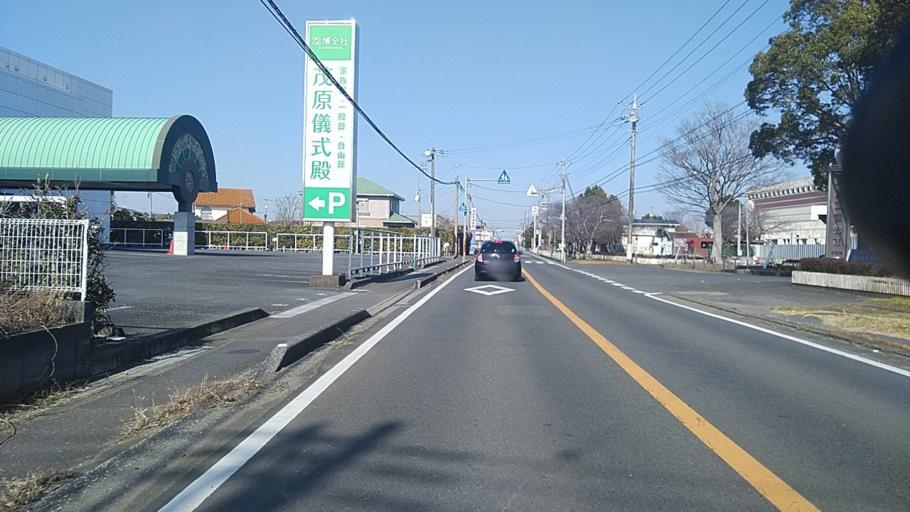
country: JP
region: Chiba
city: Mobara
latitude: 35.4376
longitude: 140.2939
